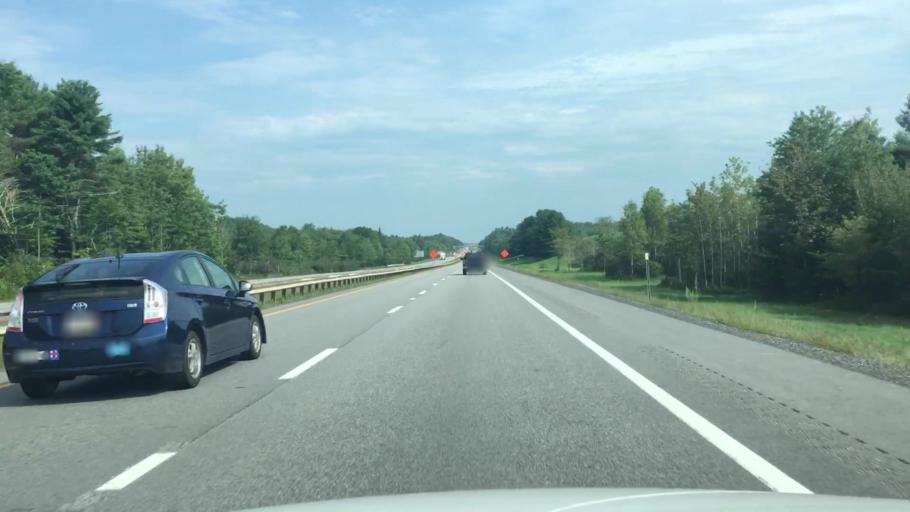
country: US
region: Maine
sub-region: Cumberland County
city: New Gloucester
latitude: 43.9083
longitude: -70.3398
